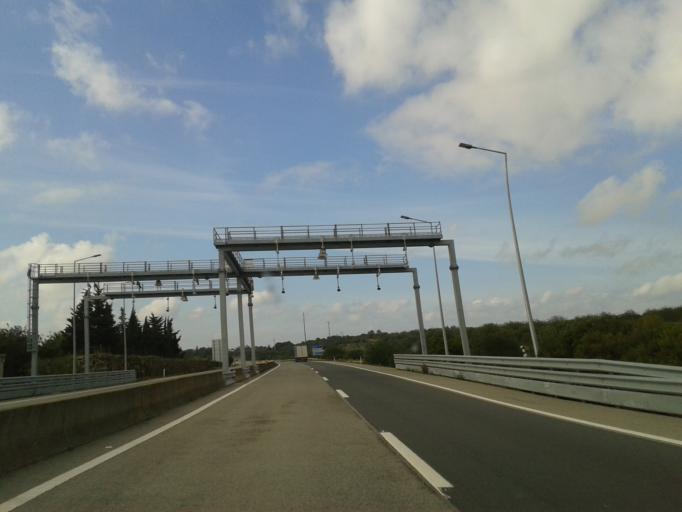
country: PT
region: Faro
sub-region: Tavira
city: Luz
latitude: 37.1343
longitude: -7.7115
